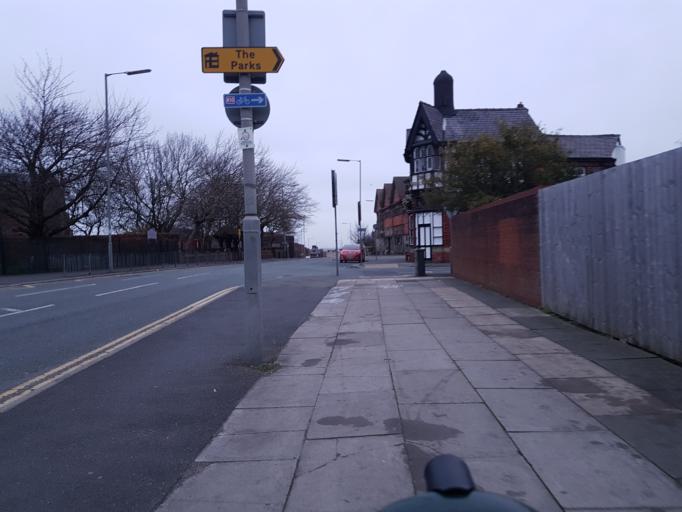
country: GB
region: England
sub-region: Liverpool
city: Liverpool
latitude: 53.4247
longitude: -2.9703
